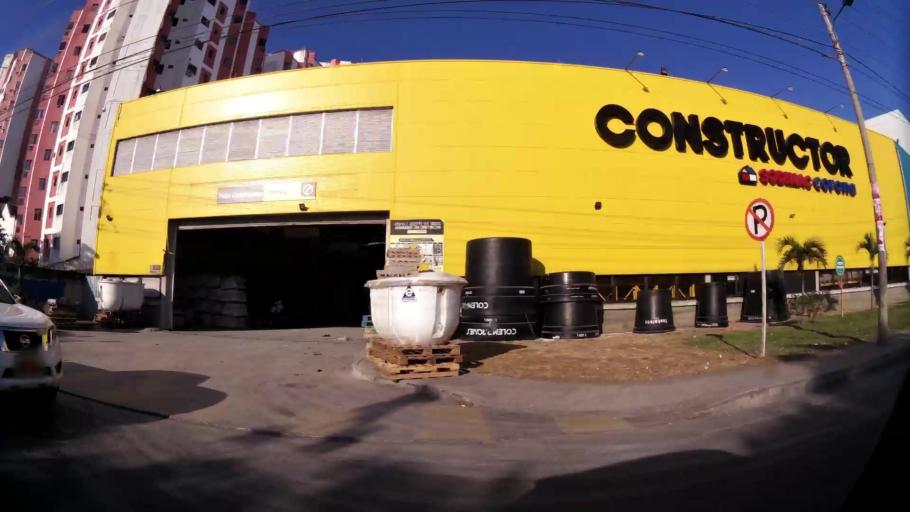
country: CO
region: Bolivar
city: Cartagena
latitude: 10.4140
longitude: -75.5309
